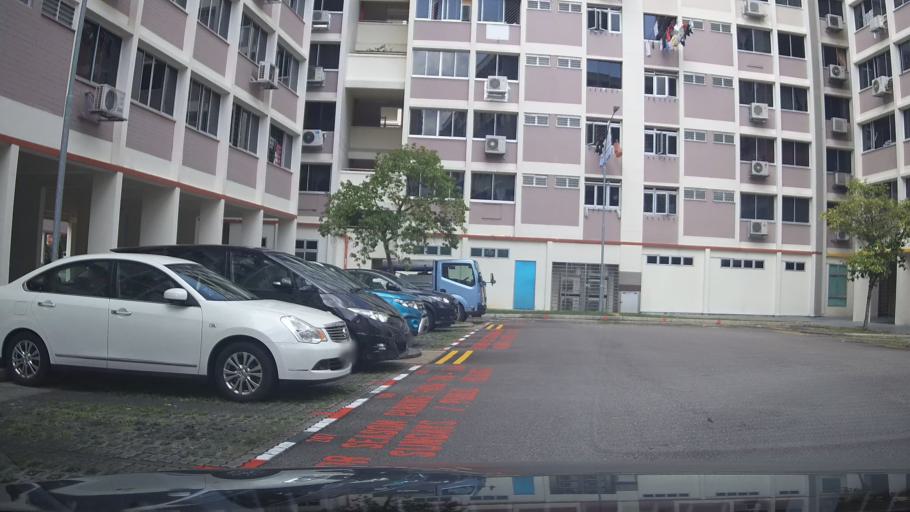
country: SG
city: Singapore
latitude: 1.3316
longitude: 103.8569
